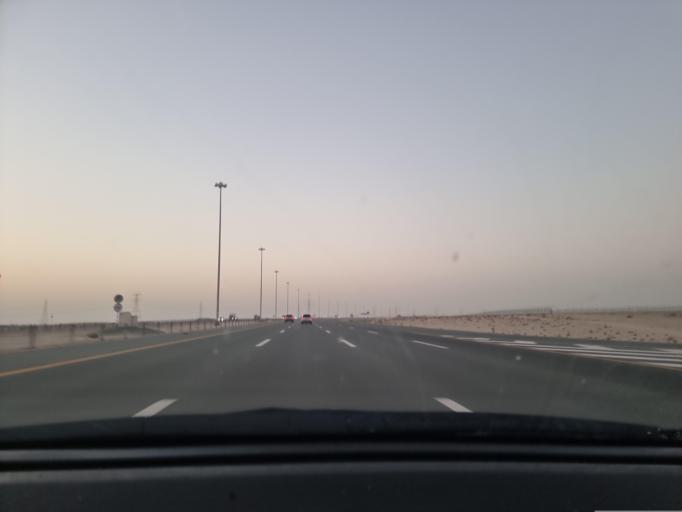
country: AE
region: Abu Dhabi
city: Abu Dhabi
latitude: 24.4443
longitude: 54.7566
